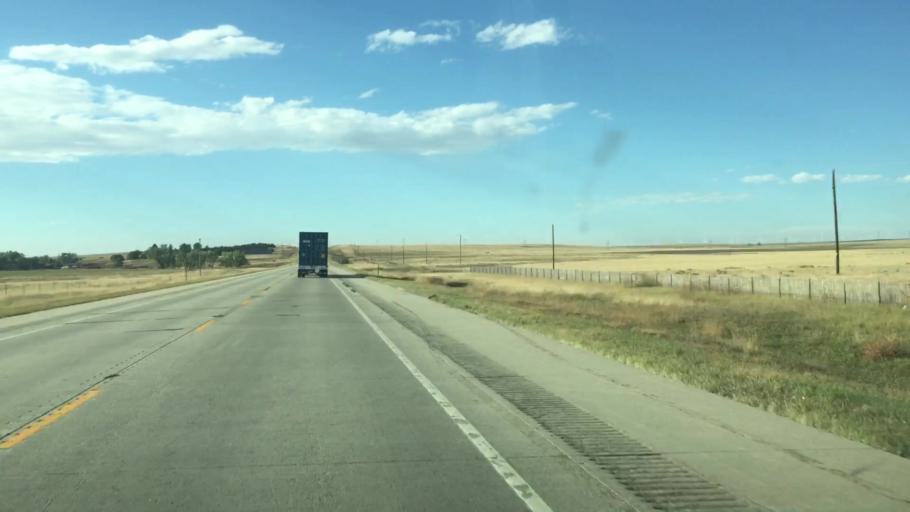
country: US
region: Colorado
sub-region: Lincoln County
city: Limon
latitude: 39.2357
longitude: -103.6209
